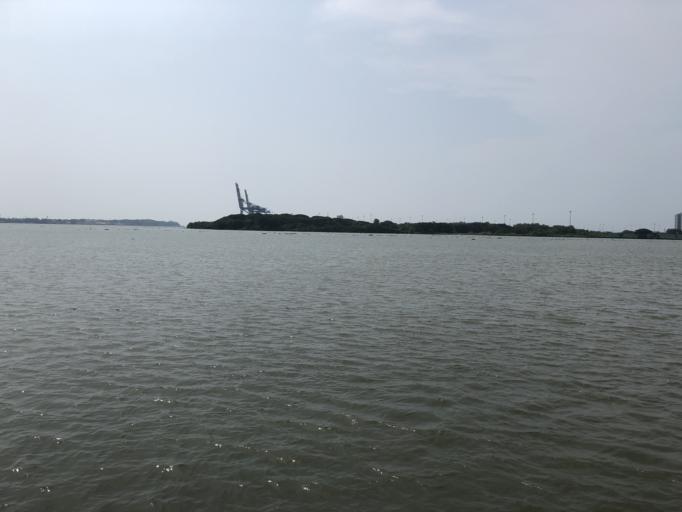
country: IN
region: Kerala
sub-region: Ernakulam
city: Cochin
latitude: 9.9848
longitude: 76.2647
